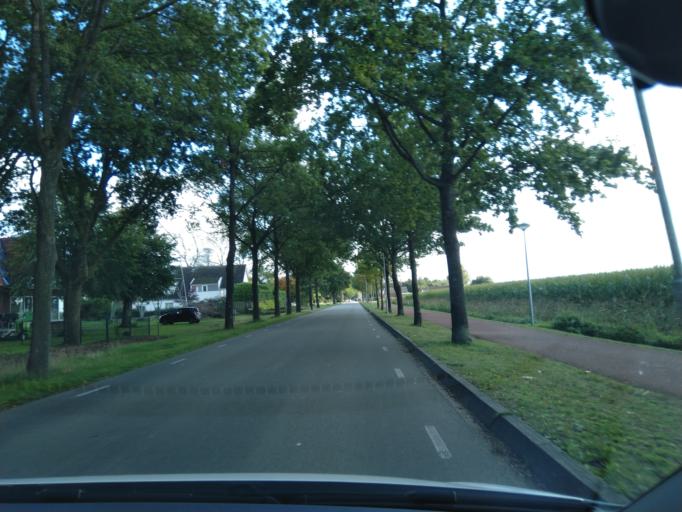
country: NL
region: Groningen
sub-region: Gemeente Veendam
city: Veendam
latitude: 53.0955
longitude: 6.9157
